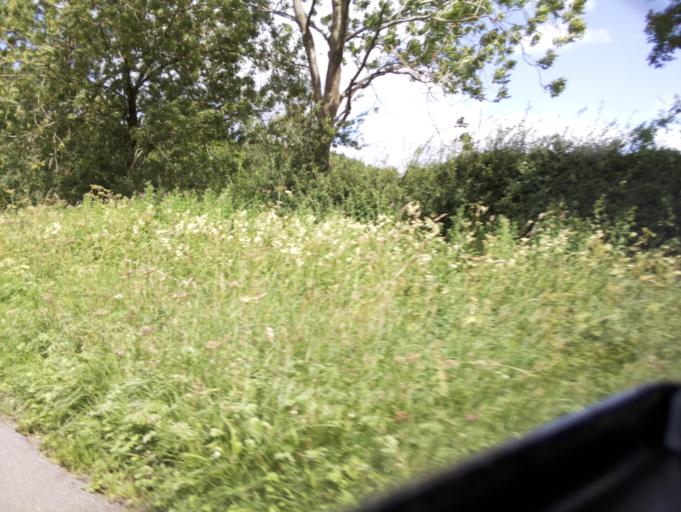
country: GB
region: England
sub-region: Nottinghamshire
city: Cotgrave
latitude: 52.8528
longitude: -1.0677
